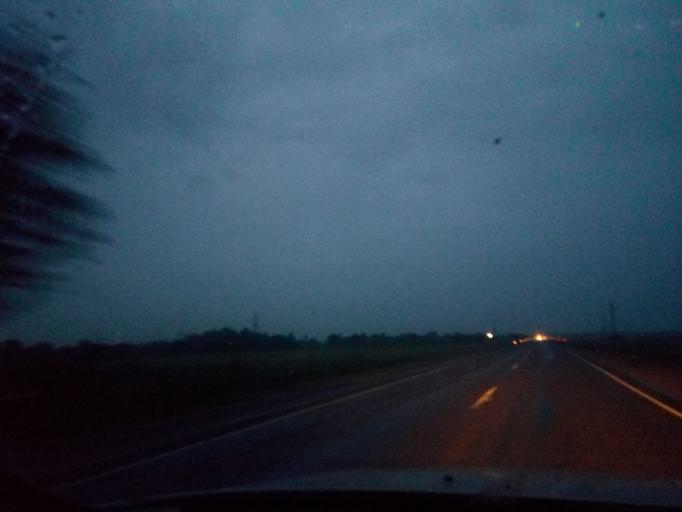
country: RU
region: Primorskiy
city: Dal'nerechensk
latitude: 45.9070
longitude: 133.7559
